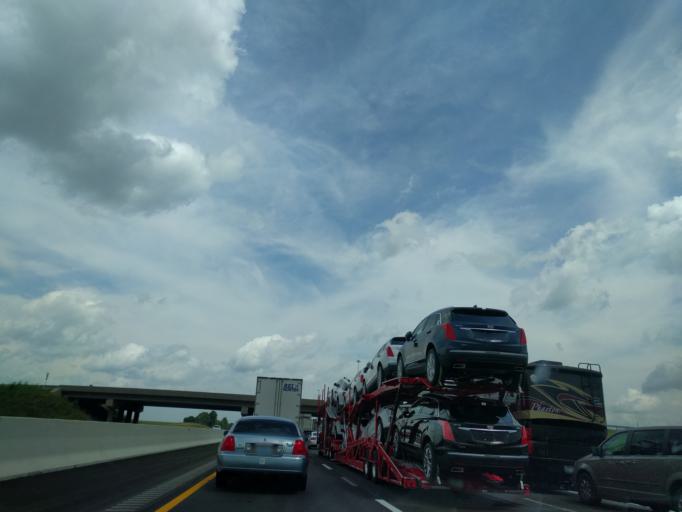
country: US
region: Kentucky
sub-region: Larue County
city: Hodgenville
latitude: 37.5206
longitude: -85.8850
